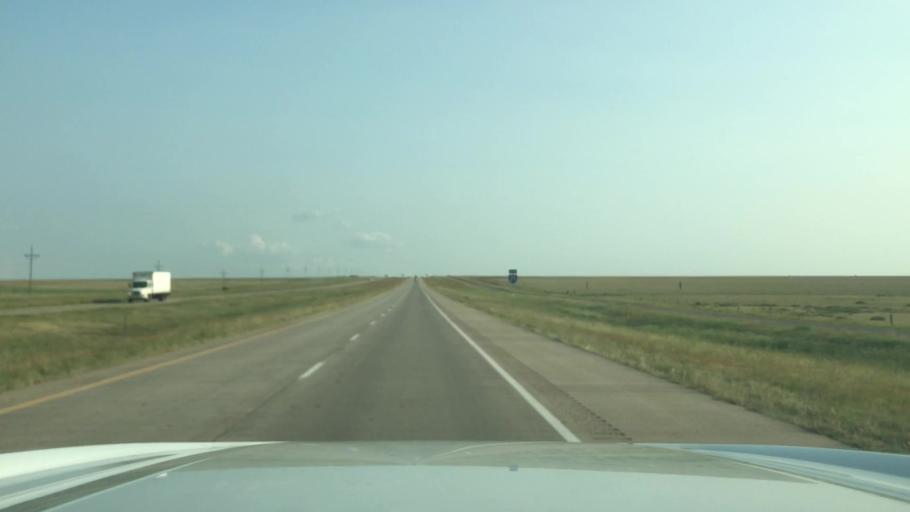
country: US
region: Texas
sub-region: Randall County
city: Canyon
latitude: 34.9322
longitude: -101.8487
